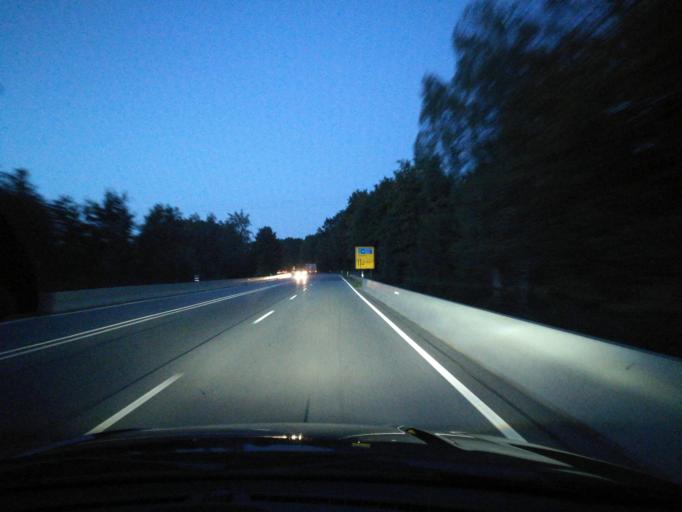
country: DE
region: Bavaria
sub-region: Lower Bavaria
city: Bad Abbach
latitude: 48.9401
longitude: 12.0421
